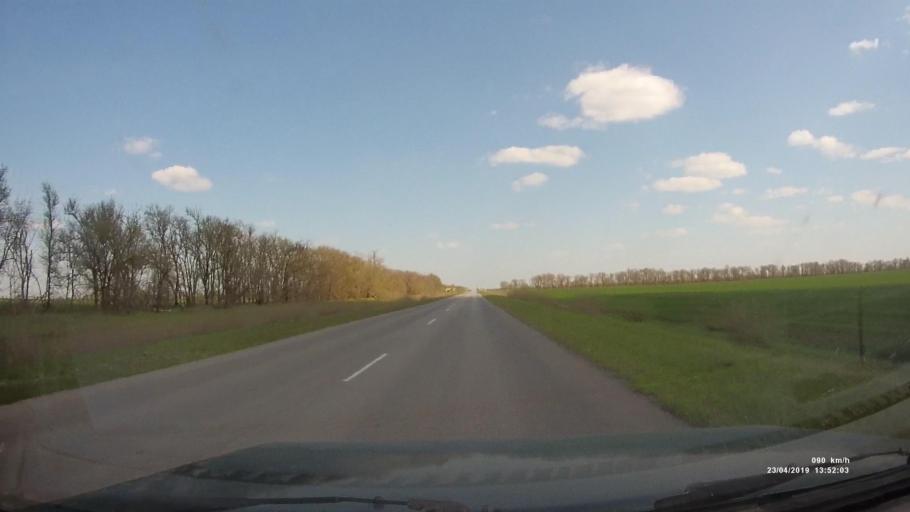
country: RU
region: Rostov
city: Remontnoye
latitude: 46.5996
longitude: 42.9478
